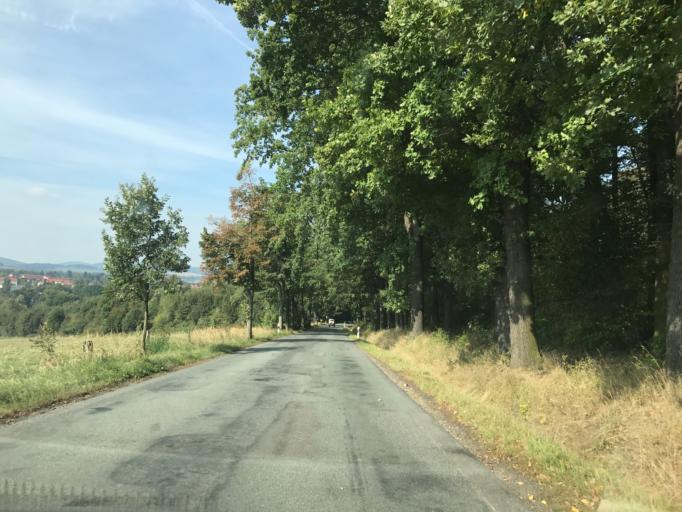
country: DE
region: Saxony
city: Lobau
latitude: 51.0865
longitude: 14.6830
